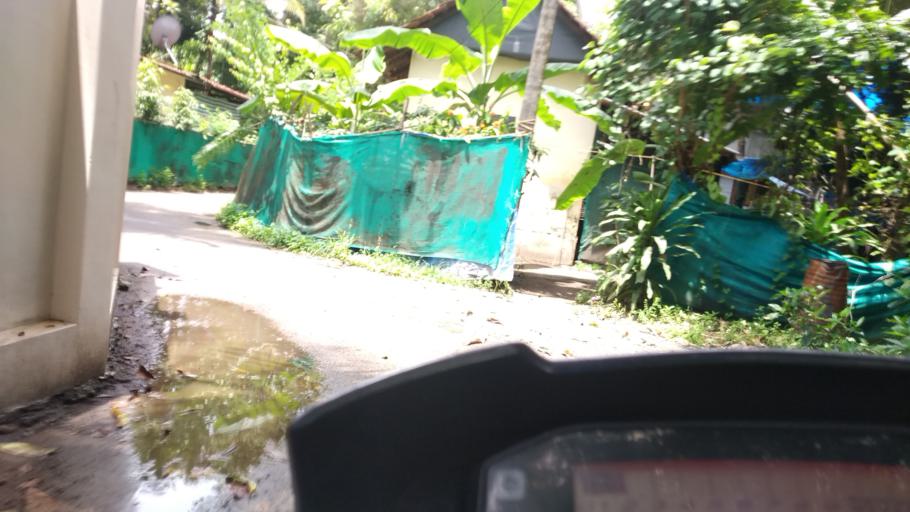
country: IN
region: Kerala
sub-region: Ernakulam
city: Elur
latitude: 10.0640
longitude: 76.2090
